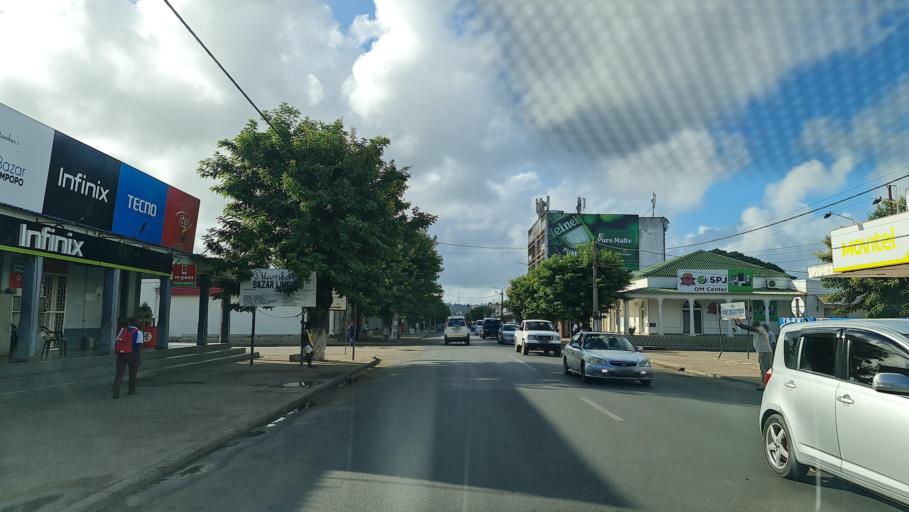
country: MZ
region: Gaza
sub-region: Xai-Xai District
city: Xai-Xai
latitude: -25.0433
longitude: 33.6421
